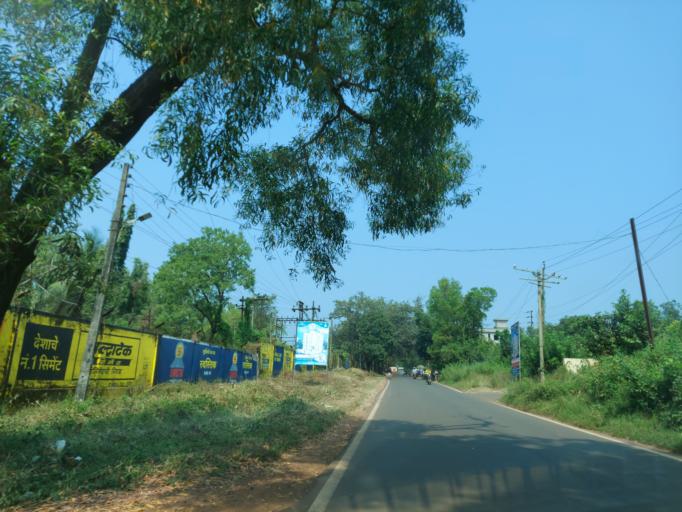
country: IN
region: Maharashtra
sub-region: Sindhudurg
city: Kudal
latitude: 15.9958
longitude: 73.6851
